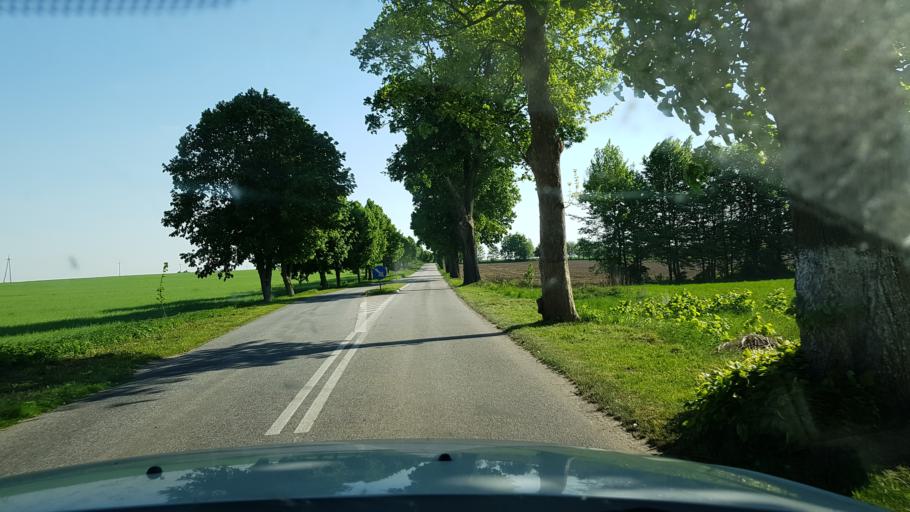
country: PL
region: West Pomeranian Voivodeship
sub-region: Powiat lobeski
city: Resko
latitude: 53.8083
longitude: 15.4195
